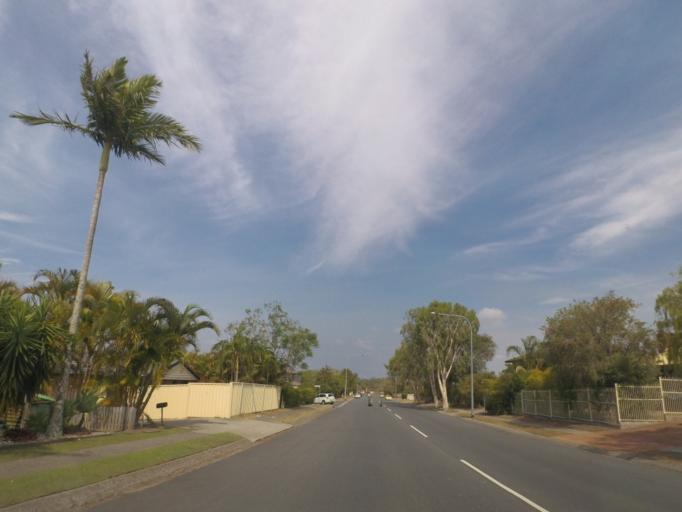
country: AU
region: Queensland
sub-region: Brisbane
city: Sunnybank Hills
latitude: -27.5997
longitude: 153.0604
